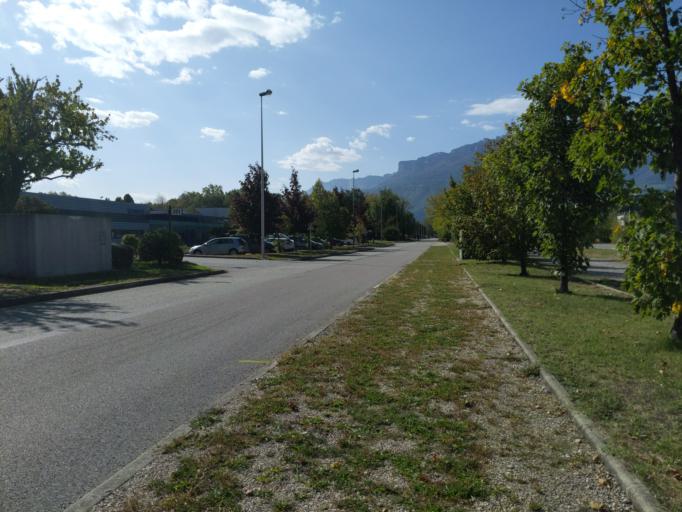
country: FR
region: Rhone-Alpes
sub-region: Departement de la Savoie
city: Montmelian
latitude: 45.4788
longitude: 6.0371
